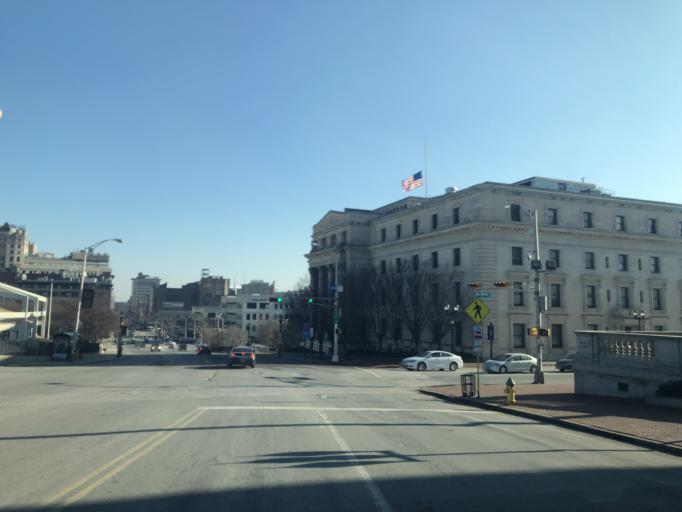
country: US
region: New Jersey
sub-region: Essex County
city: Newark
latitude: 40.7379
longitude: -74.1796
